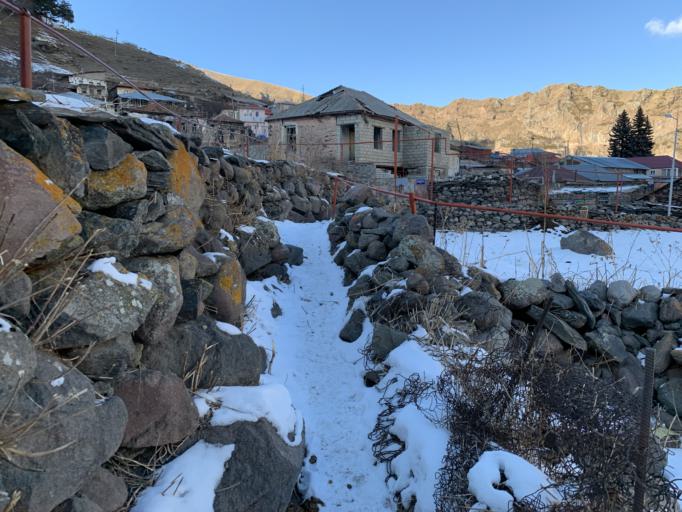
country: GE
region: Mtskheta-Mtianeti
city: Step'antsminda
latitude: 42.6621
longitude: 44.6299
